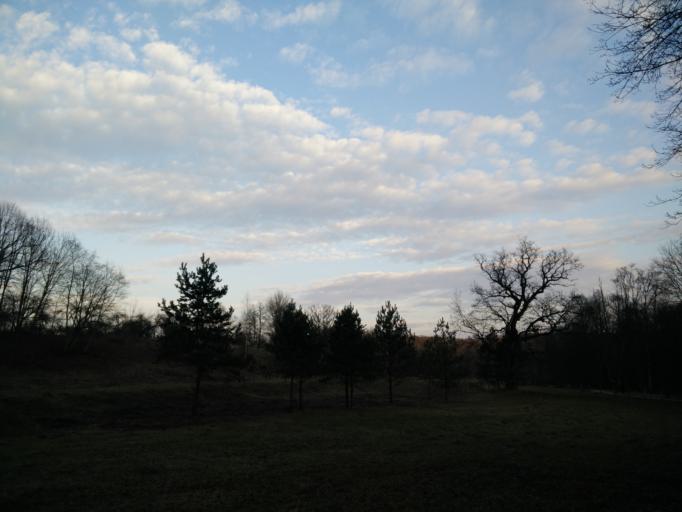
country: LT
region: Vilnius County
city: Rasos
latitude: 54.6878
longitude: 25.3531
